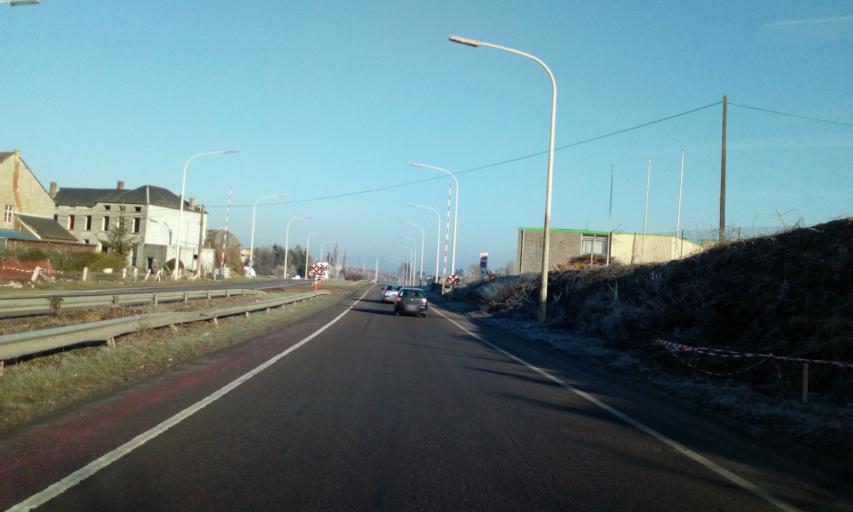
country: BE
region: Wallonia
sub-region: Province de Namur
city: Couvin
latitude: 50.0735
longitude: 4.5101
